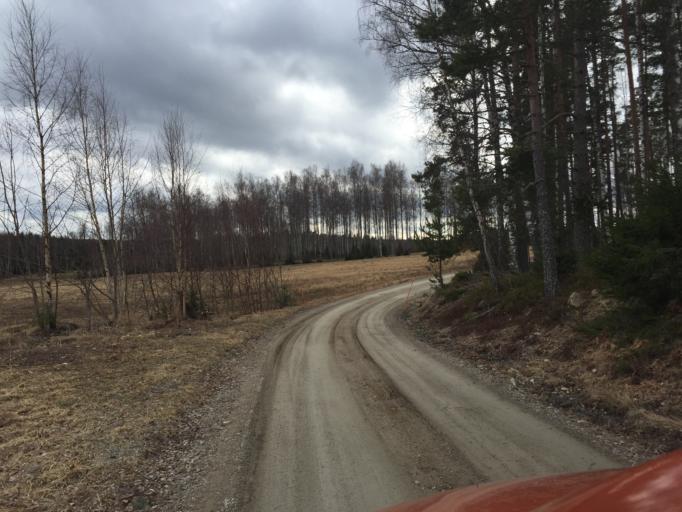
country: SE
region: Soedermanland
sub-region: Vingakers Kommun
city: Vingaker
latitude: 58.9966
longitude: 15.7197
